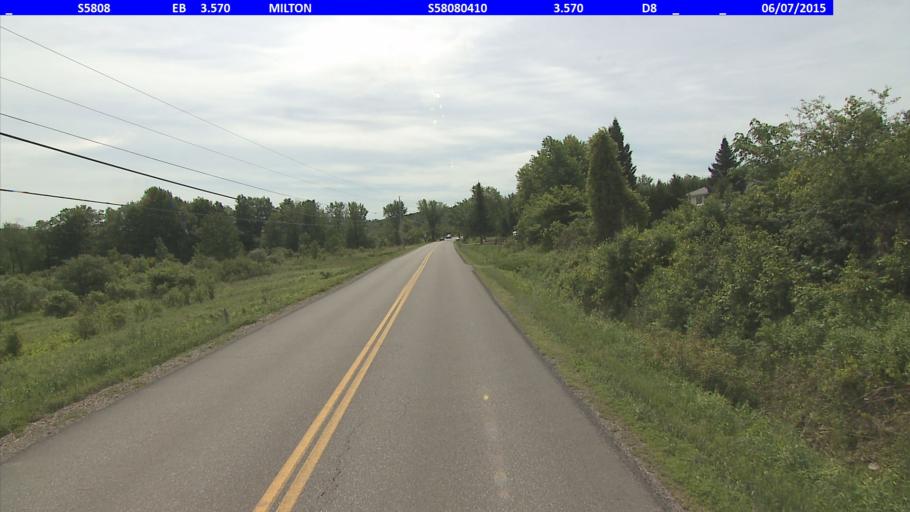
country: US
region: Vermont
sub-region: Chittenden County
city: Milton
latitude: 44.6367
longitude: -73.0511
